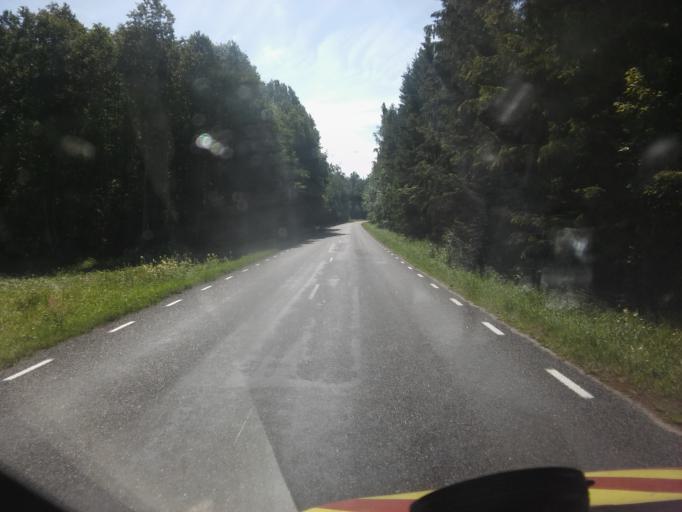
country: EE
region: Paernumaa
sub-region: Paikuse vald
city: Paikuse
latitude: 58.2974
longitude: 24.6885
